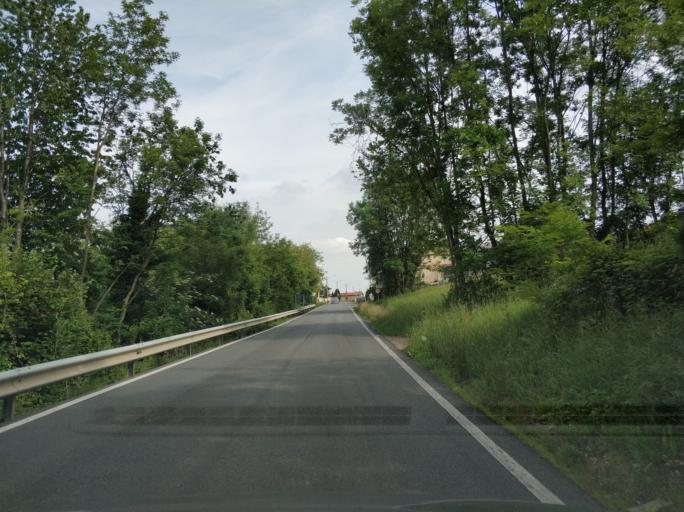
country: IT
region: Piedmont
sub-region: Provincia di Torino
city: Corio
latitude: 45.2953
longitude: 7.5479
